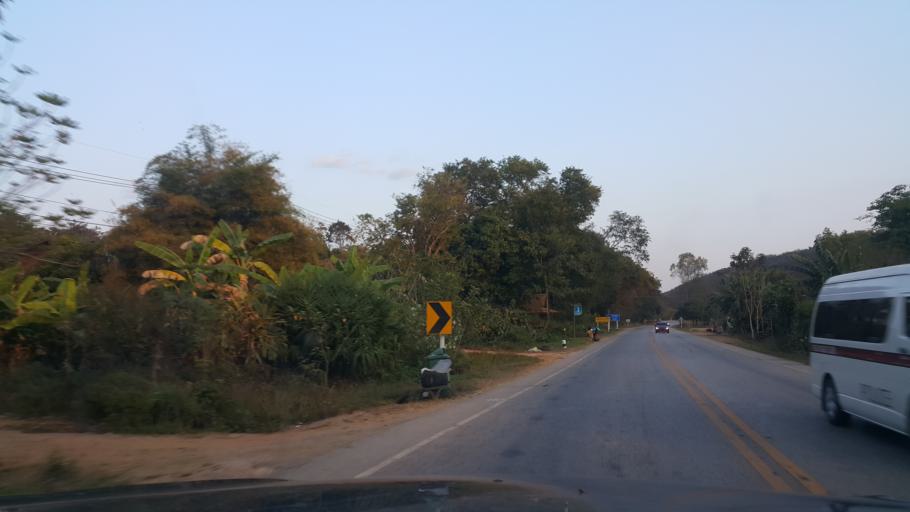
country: TH
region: Loei
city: Loei
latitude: 17.4743
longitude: 101.5705
